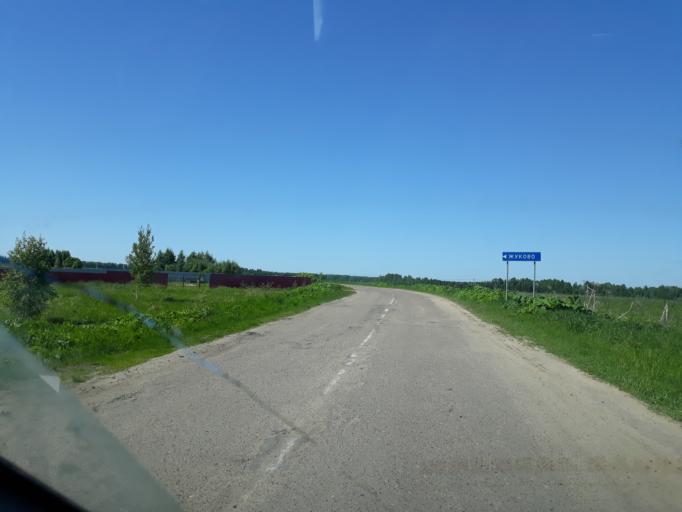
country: RU
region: Jaroslavl
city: Yaroslavl
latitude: 57.6787
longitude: 40.0185
